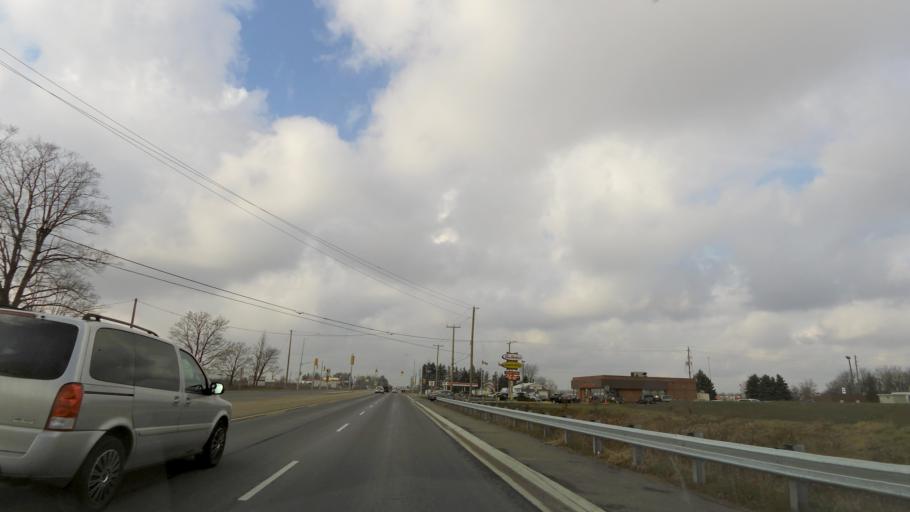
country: CA
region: Ontario
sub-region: Wellington County
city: Guelph
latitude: 43.4574
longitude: -80.1303
